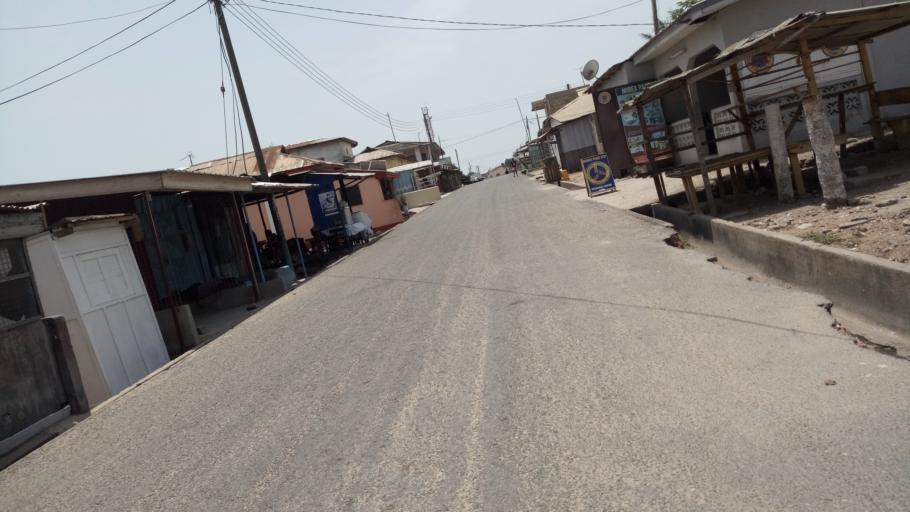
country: GH
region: Central
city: Winneba
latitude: 5.3456
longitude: -0.6250
